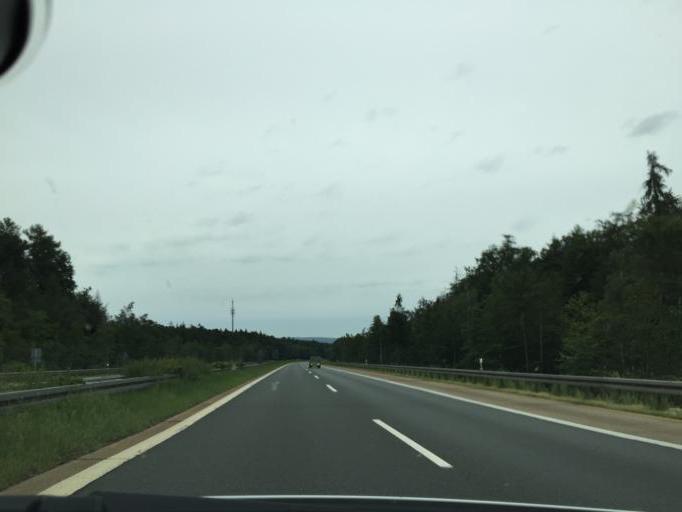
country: DE
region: Bavaria
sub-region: Regierungsbezirk Unterfranken
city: Oberthulba
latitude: 50.2129
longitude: 9.9183
